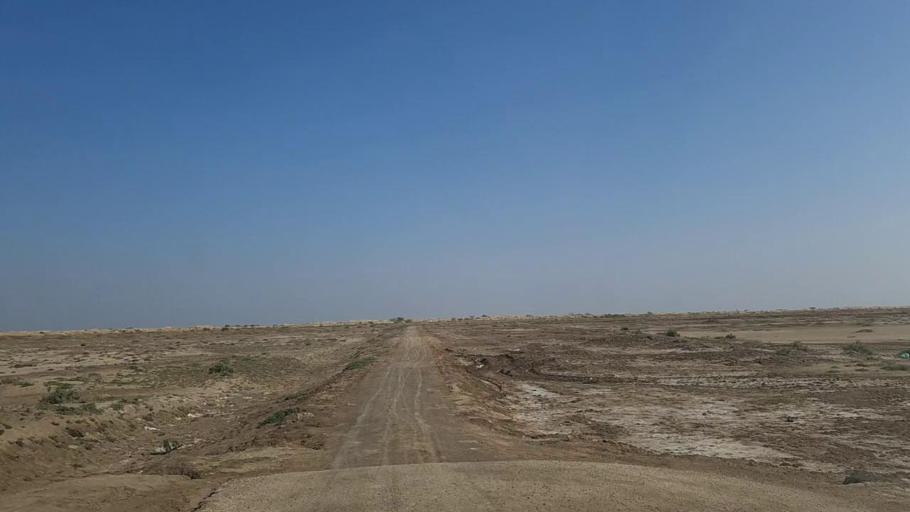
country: PK
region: Sindh
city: Digri
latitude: 25.0710
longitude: 69.2262
